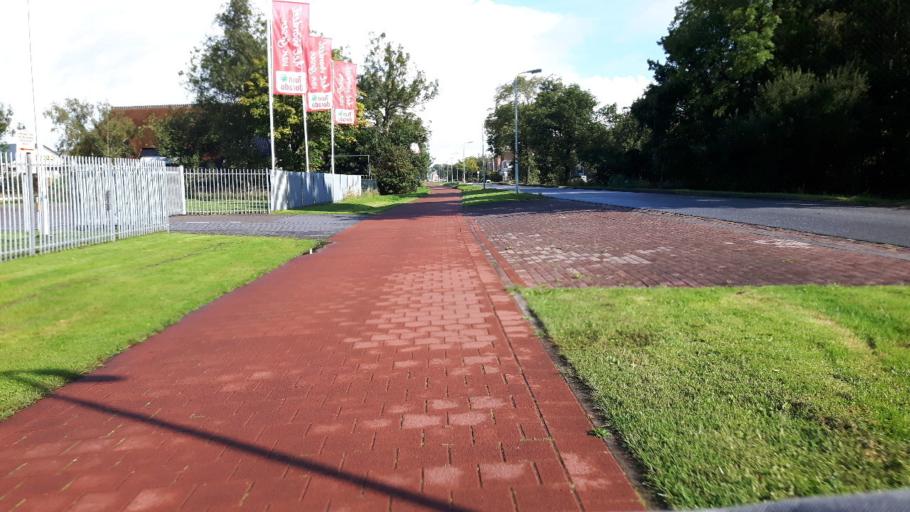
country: NL
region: Friesland
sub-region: Gemeente Smallingerland
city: Drachten
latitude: 53.0860
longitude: 6.0998
